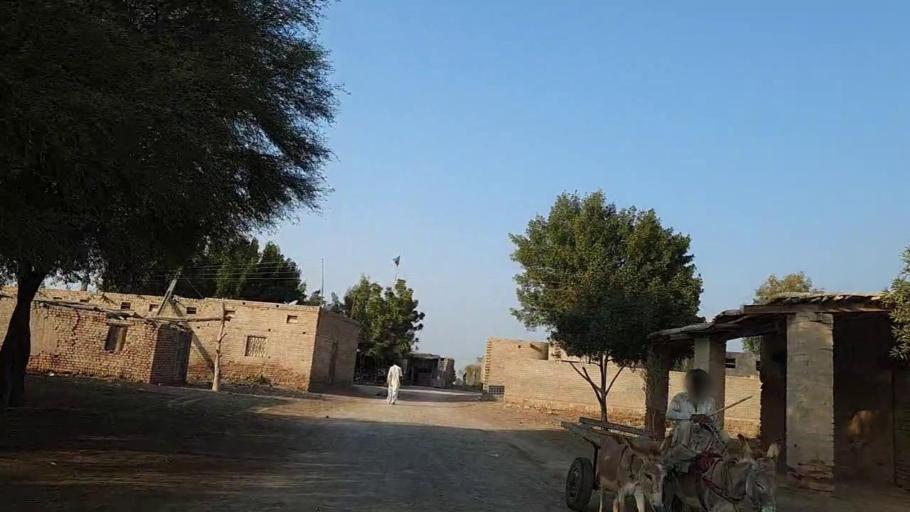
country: PK
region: Sindh
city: Sakrand
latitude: 26.1145
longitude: 68.3686
